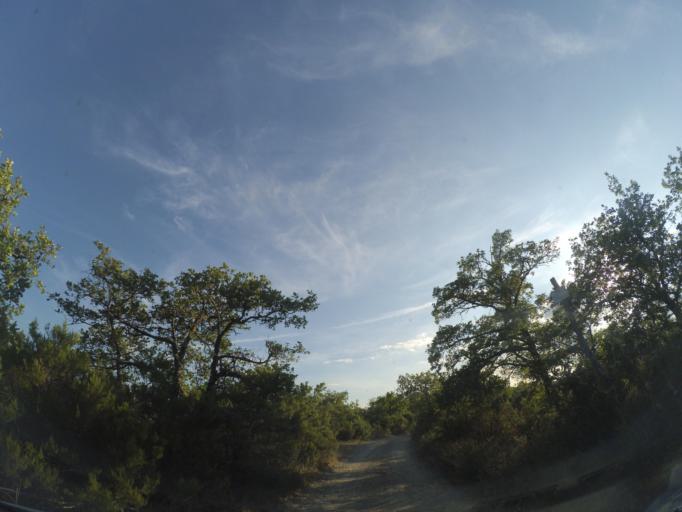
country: IT
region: Tuscany
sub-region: Province of Arezzo
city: Castiglion Fibocchi
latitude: 43.5440
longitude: 11.7870
